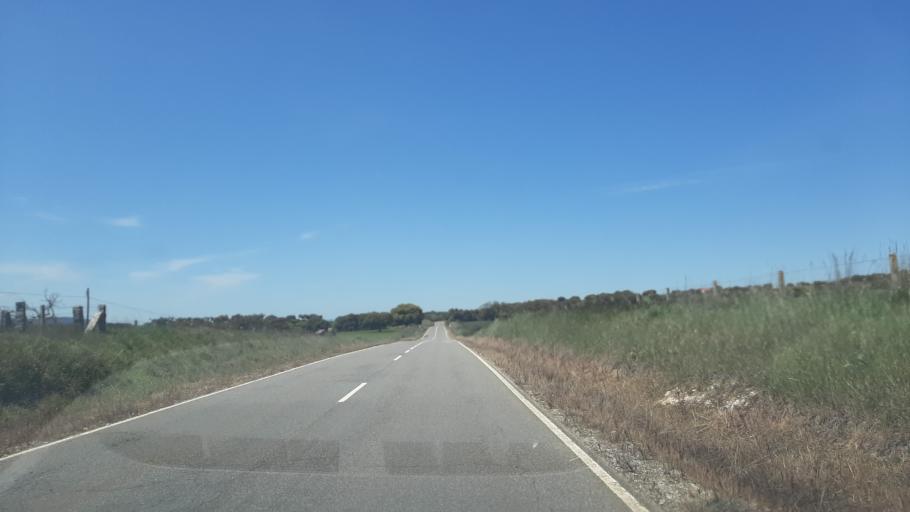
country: ES
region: Castille and Leon
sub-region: Provincia de Salamanca
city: Puente del Congosto
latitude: 40.5357
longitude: -5.5377
